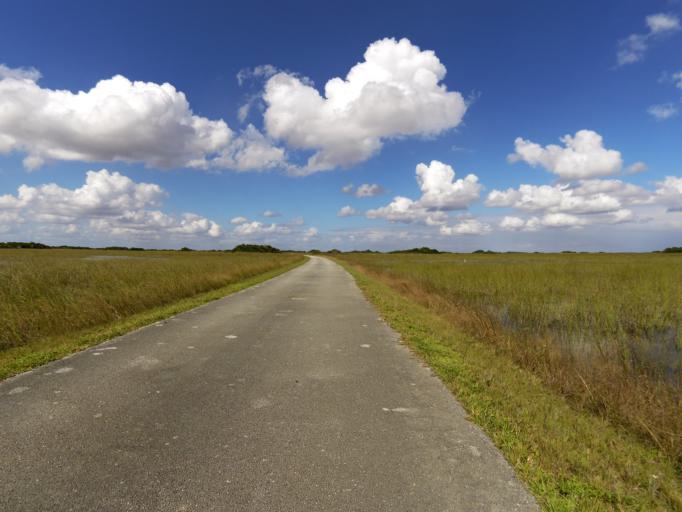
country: US
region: Florida
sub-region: Miami-Dade County
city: The Hammocks
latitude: 25.6824
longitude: -80.7625
